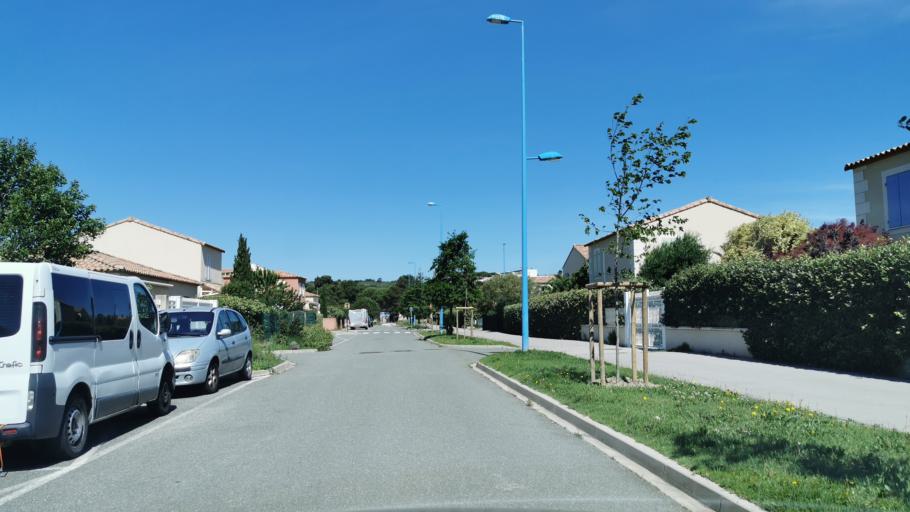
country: FR
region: Languedoc-Roussillon
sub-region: Departement de l'Aude
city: Armissan
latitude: 43.1579
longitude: 3.1626
